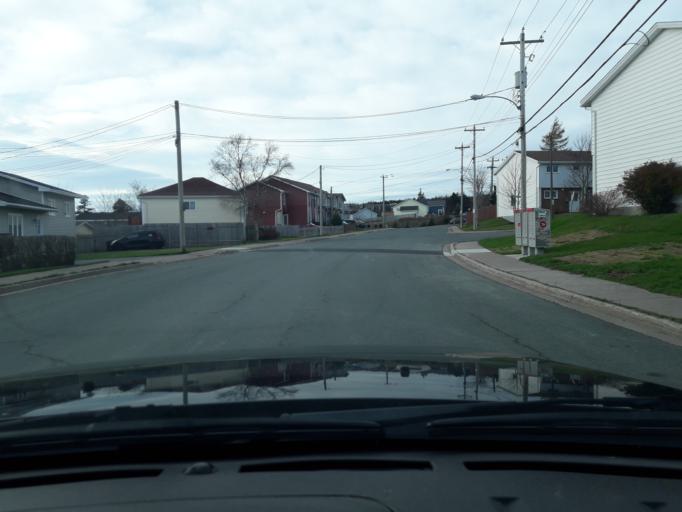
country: CA
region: Newfoundland and Labrador
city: St. John's
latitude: 47.5649
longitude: -52.7611
